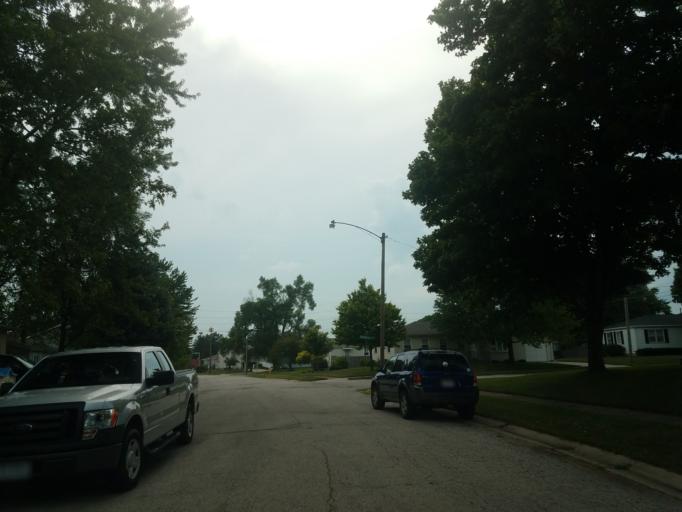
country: US
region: Illinois
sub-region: McLean County
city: Bloomington
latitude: 40.4635
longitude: -88.9709
